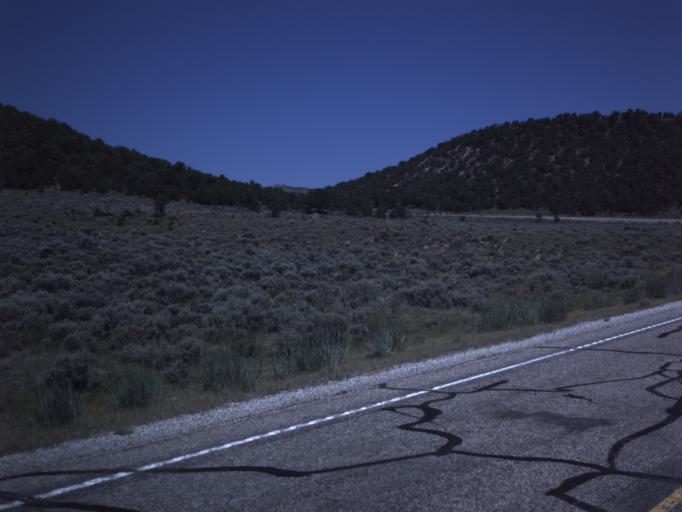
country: US
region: Utah
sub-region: Wayne County
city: Loa
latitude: 38.6425
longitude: -111.4333
